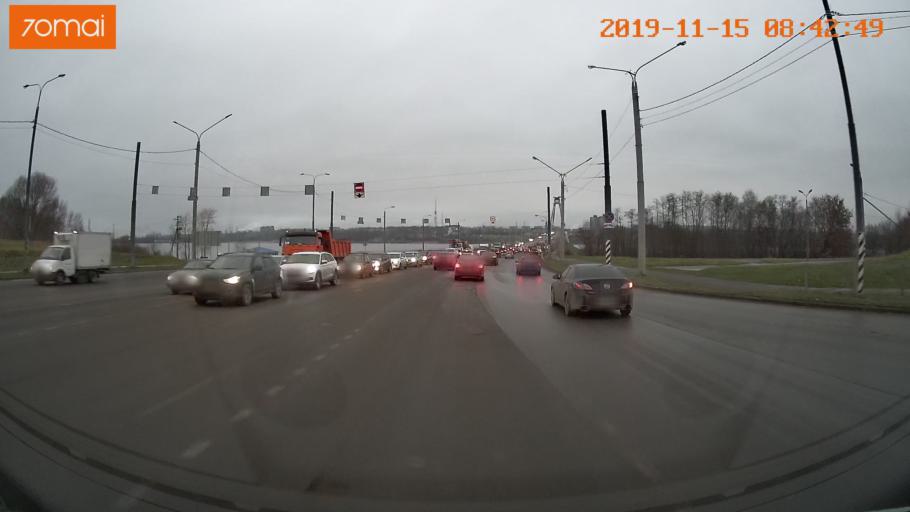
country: RU
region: Vologda
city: Cherepovets
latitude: 59.1058
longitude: 37.9060
